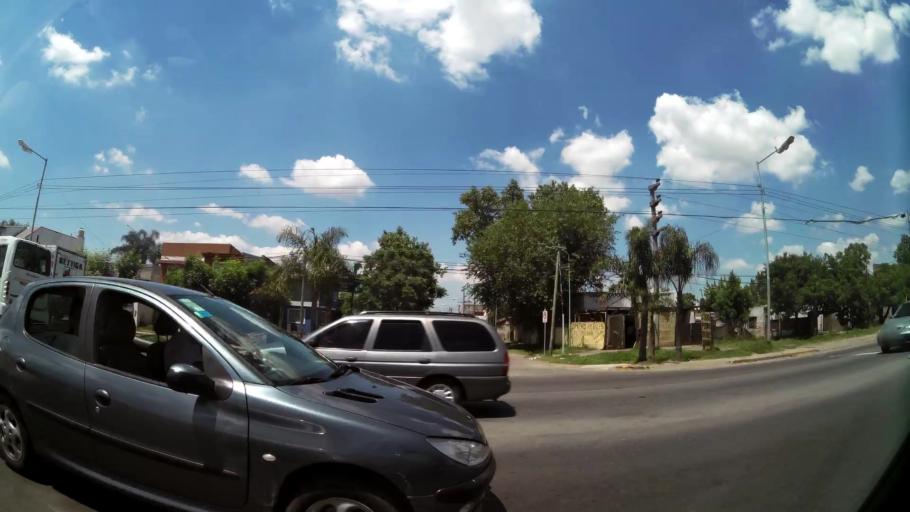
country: AR
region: Buenos Aires
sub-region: Partido de Tigre
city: Tigre
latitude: -34.4430
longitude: -58.5923
